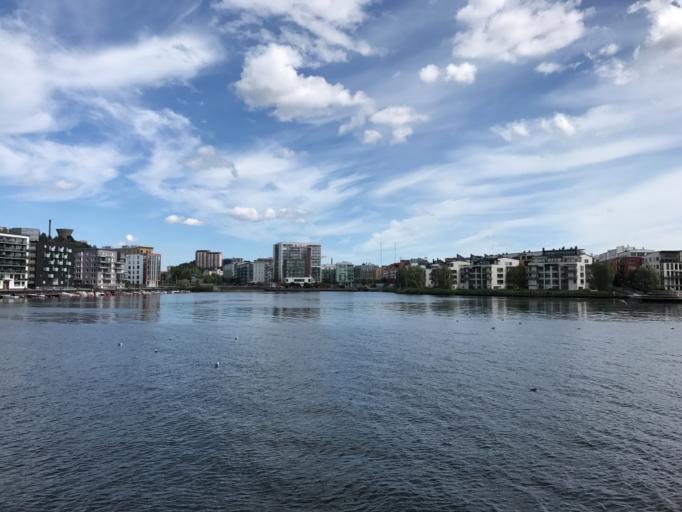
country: SE
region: Stockholm
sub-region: Stockholms Kommun
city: OEstermalm
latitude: 59.3074
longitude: 18.0993
